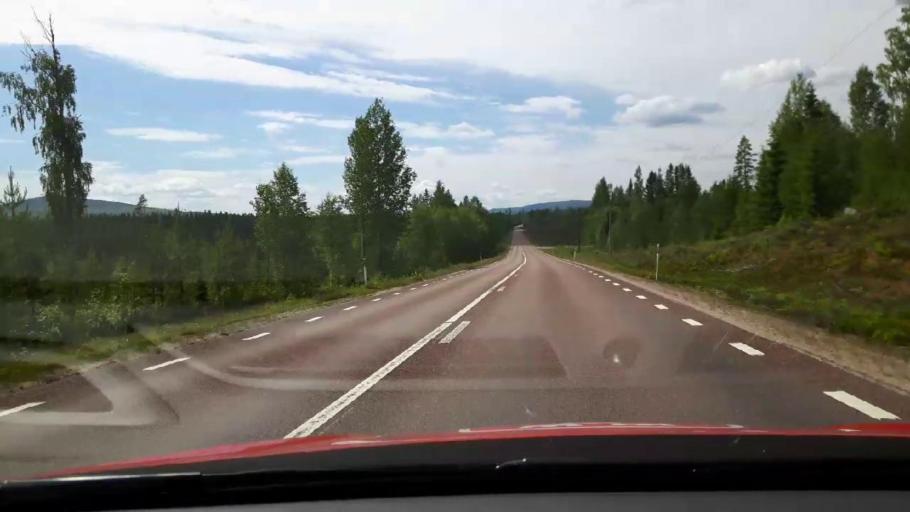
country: SE
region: Jaemtland
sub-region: Harjedalens Kommun
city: Sveg
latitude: 62.0605
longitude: 14.9124
